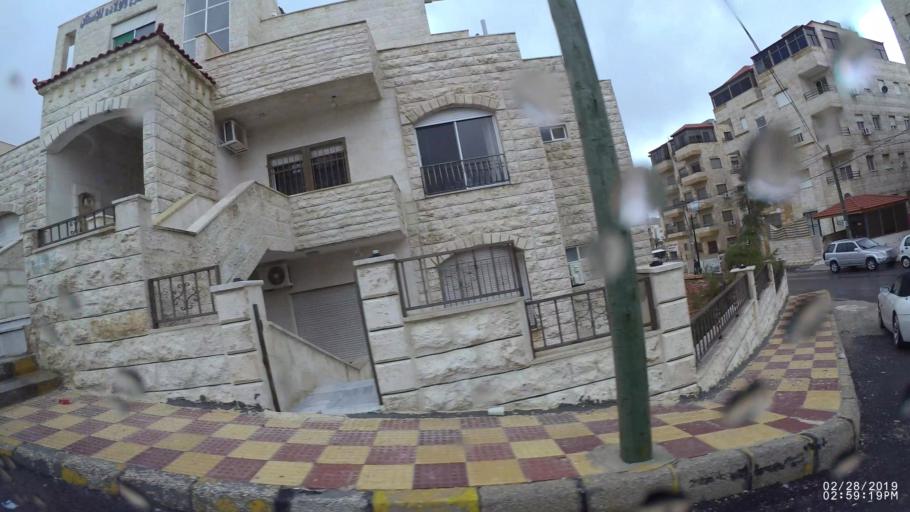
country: JO
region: Amman
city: Al Jubayhah
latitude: 32.0274
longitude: 35.8696
